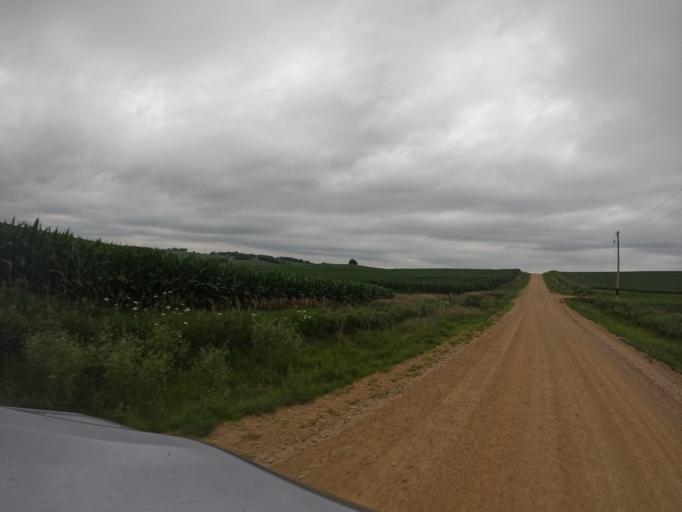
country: US
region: Iowa
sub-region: Jackson County
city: Maquoketa
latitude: 41.9470
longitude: -90.6454
